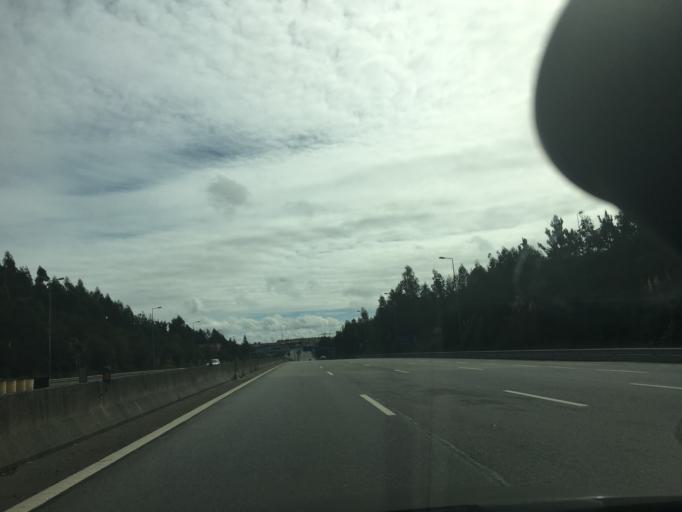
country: PT
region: Porto
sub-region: Matosinhos
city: Santa Cruz do Bispo
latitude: 41.2224
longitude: -8.6615
